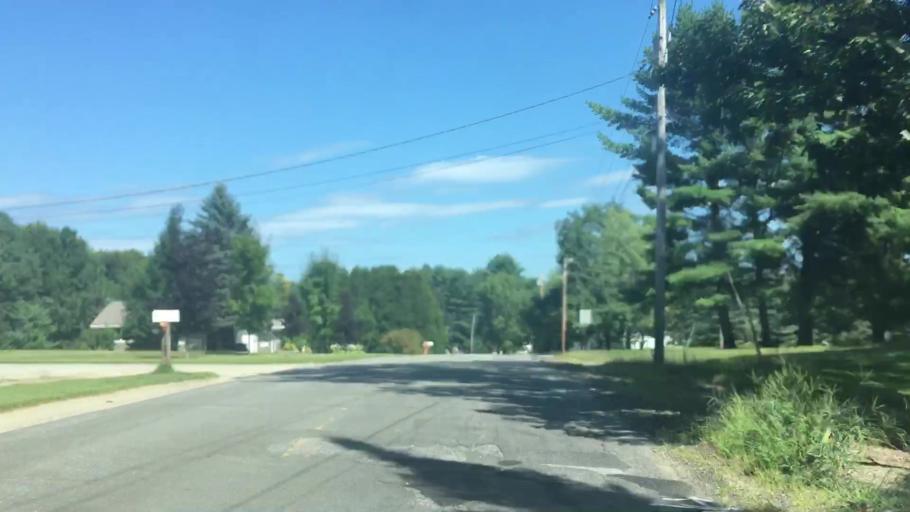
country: US
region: Maine
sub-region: Androscoggin County
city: Lisbon
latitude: 44.0640
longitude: -70.1164
